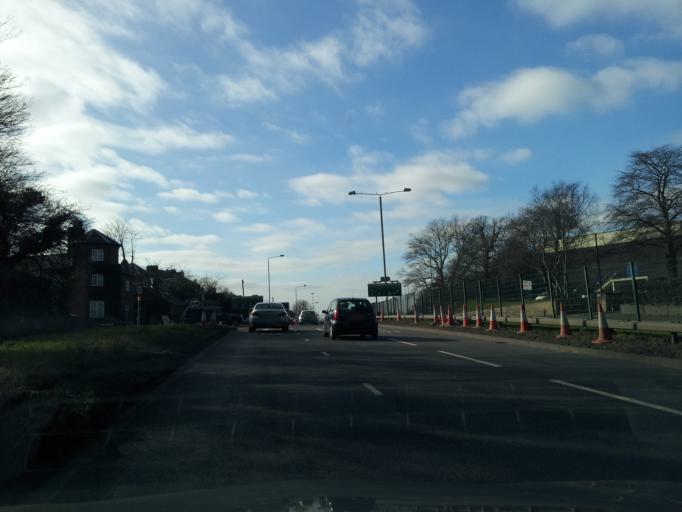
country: GB
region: England
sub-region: Derbyshire
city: Long Eaton
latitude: 52.9371
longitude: -1.2463
